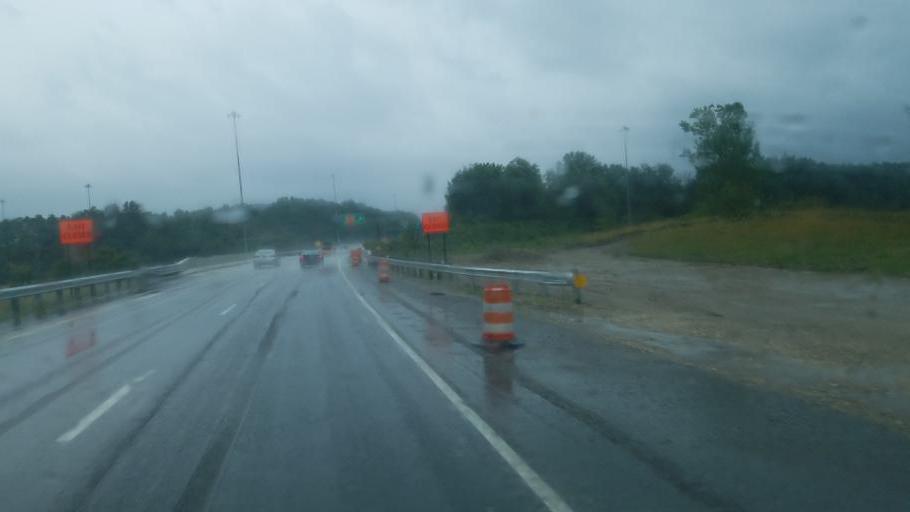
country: US
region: Ohio
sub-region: Trumbull County
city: Churchill
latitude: 41.1498
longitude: -80.6754
